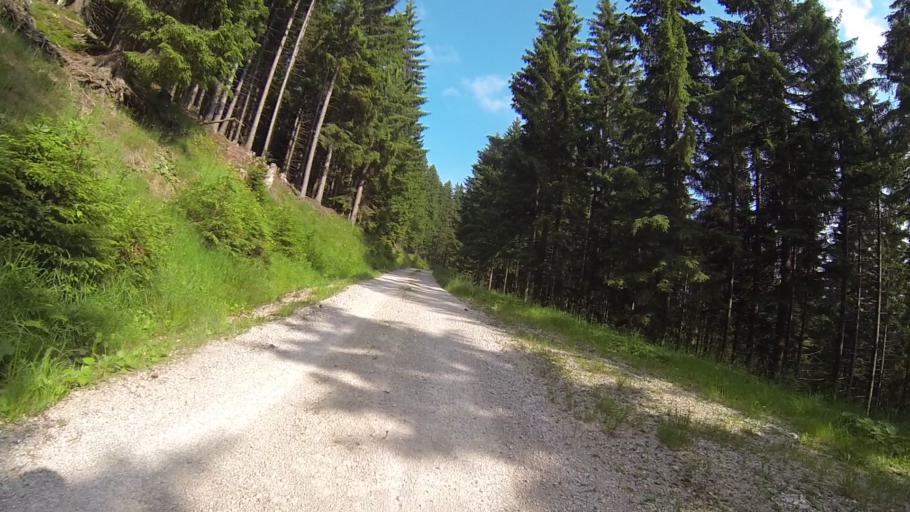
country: DE
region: Bavaria
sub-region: Swabia
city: Nesselwang
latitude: 47.5867
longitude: 10.4969
